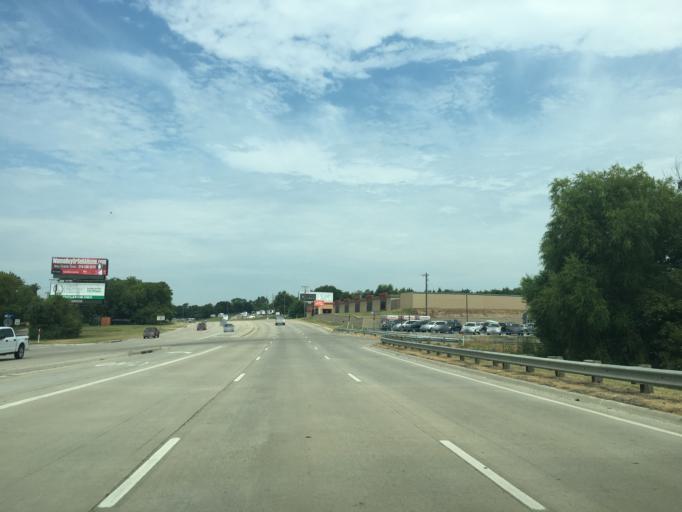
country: US
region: Texas
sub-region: Collin County
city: Lavon
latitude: 33.0255
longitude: -96.4830
